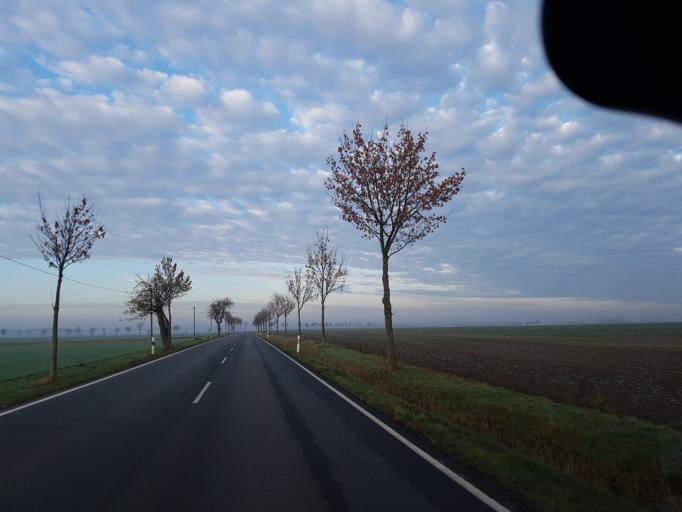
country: DE
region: Saxony-Anhalt
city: Zahna
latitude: 51.9035
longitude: 12.8244
